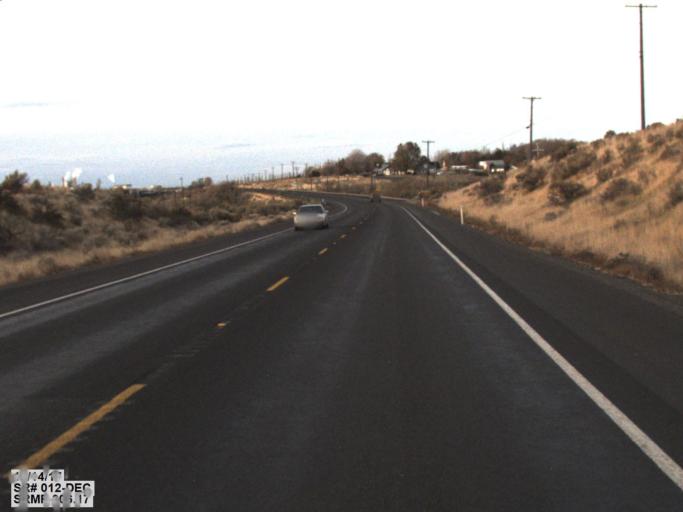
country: US
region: Washington
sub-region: Benton County
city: Finley
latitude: 46.0767
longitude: -118.9077
